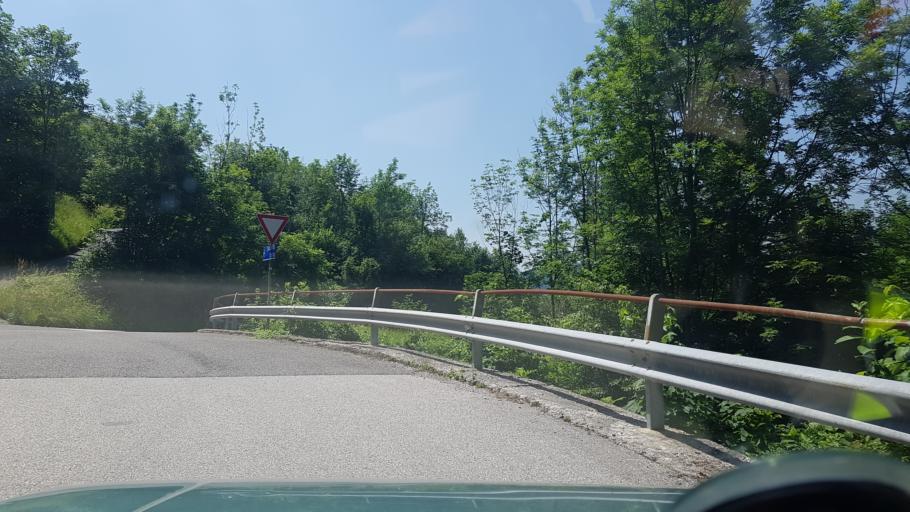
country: IT
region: Friuli Venezia Giulia
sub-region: Provincia di Udine
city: Lusevera
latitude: 46.2547
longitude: 13.2781
